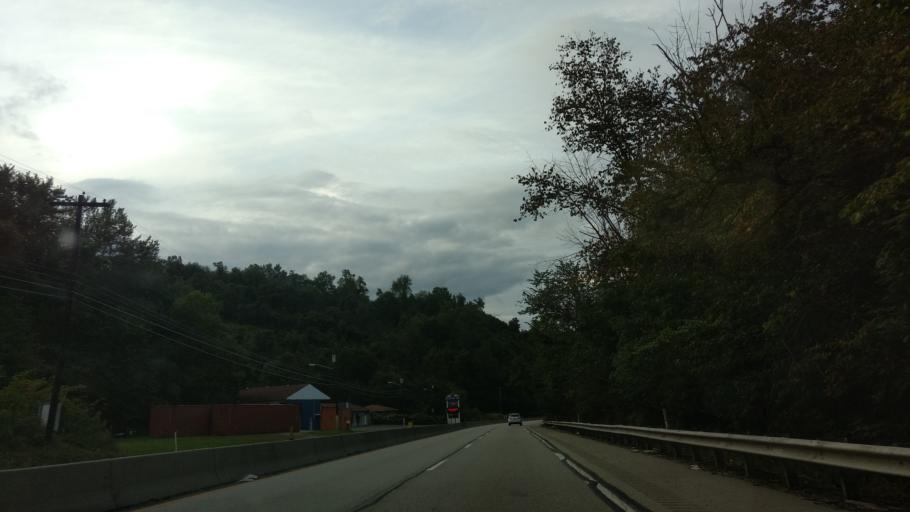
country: US
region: Pennsylvania
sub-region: Allegheny County
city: Elizabeth
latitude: 40.2542
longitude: -79.8787
